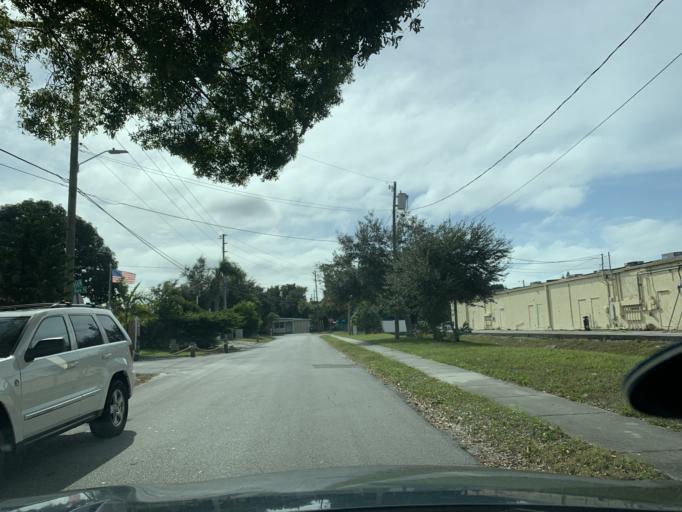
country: US
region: Florida
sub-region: Pinellas County
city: Ridgecrest
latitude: 27.8800
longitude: -82.7859
